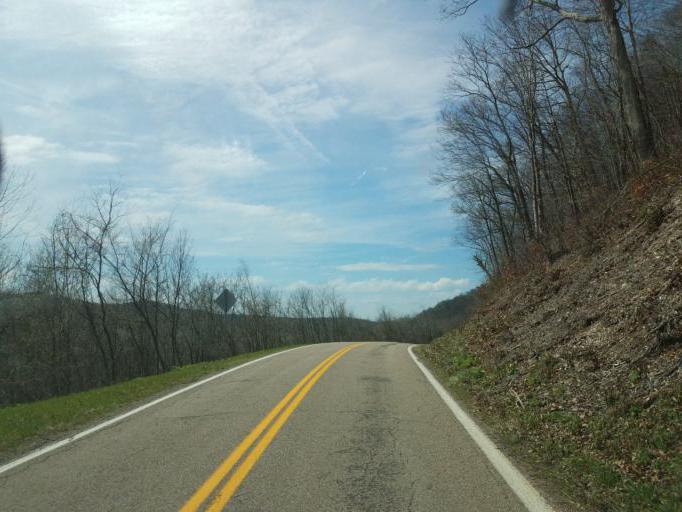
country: US
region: Ohio
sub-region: Knox County
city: Oak Hill
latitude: 40.3757
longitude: -82.1907
